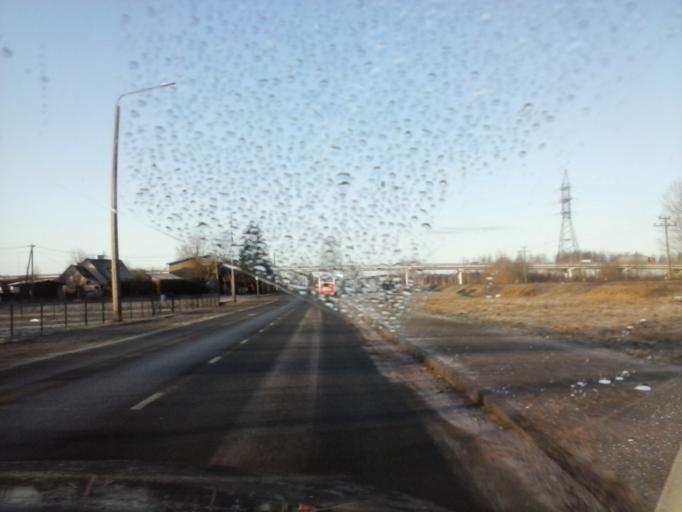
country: EE
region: Tartu
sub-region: Tartu linn
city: Tartu
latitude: 58.3495
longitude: 26.6990
